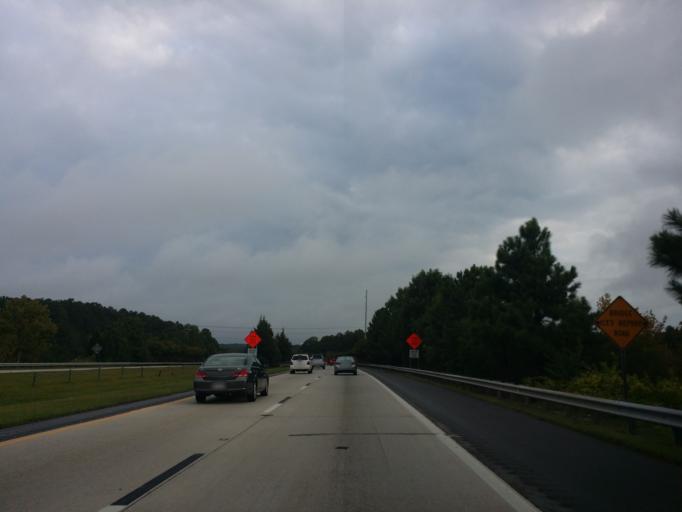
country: US
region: North Carolina
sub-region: Durham County
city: Durham
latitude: 35.9379
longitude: -78.8588
